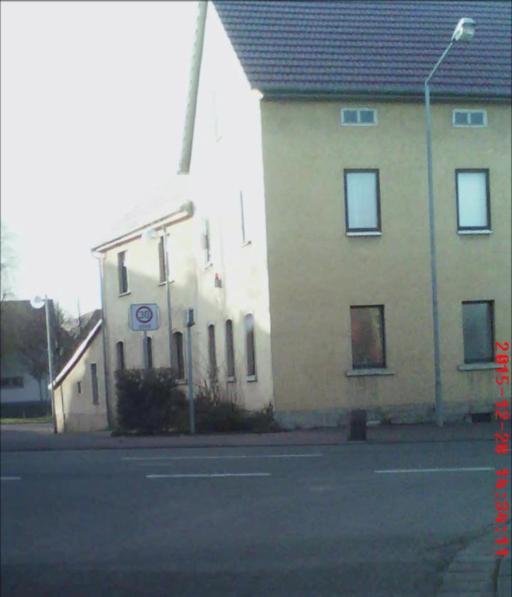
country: DE
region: Thuringia
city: Grossobringen
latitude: 51.0326
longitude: 11.3372
